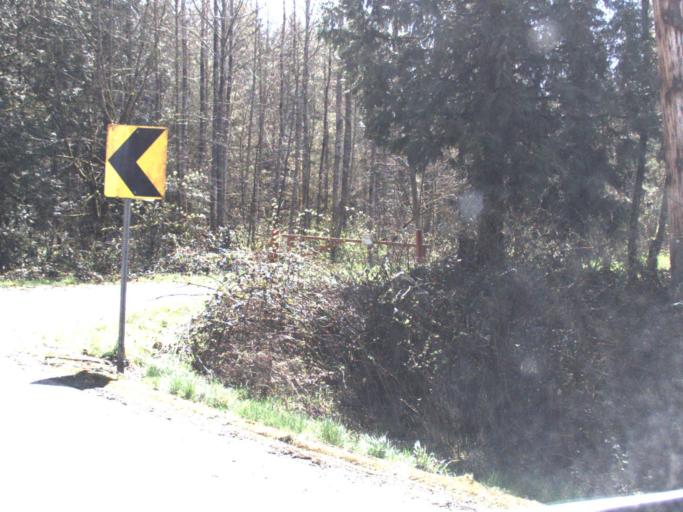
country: US
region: Washington
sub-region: King County
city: Black Diamond
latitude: 47.2690
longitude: -121.9929
